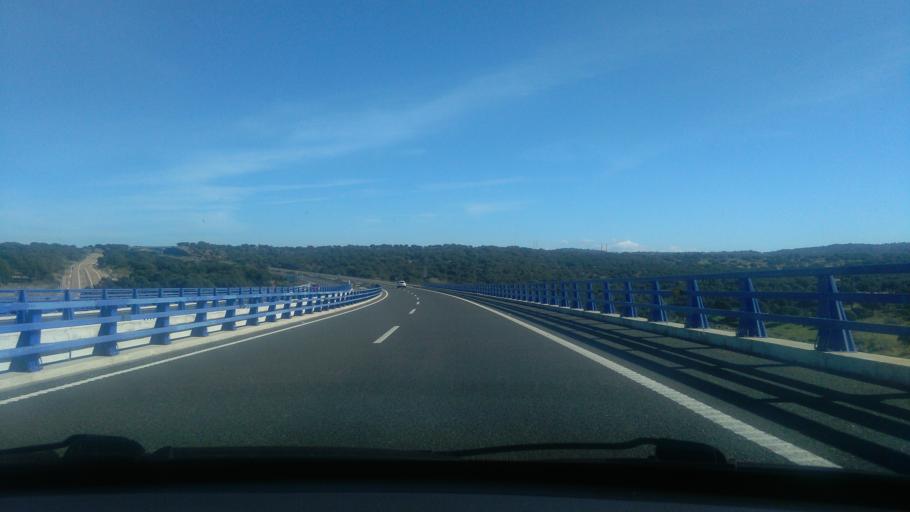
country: ES
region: Extremadura
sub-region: Provincia de Caceres
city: Plasenzuela
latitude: 39.4350
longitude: -6.0909
